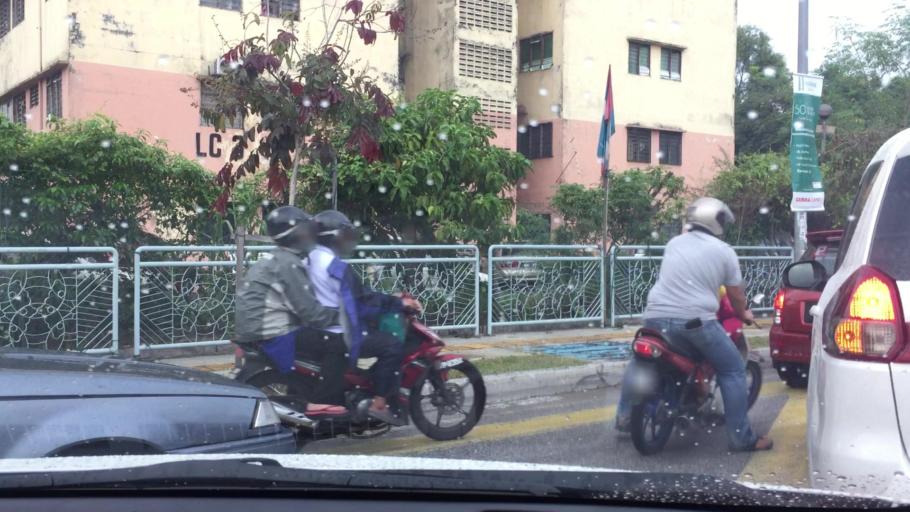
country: MY
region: Selangor
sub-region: Petaling
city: Petaling Jaya
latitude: 3.0741
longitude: 101.6440
